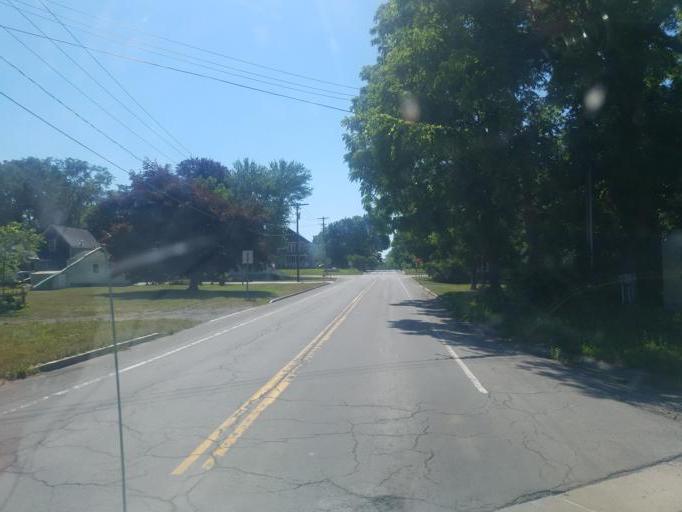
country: US
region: New York
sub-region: Ontario County
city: Phelps
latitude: 42.9325
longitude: -77.0116
